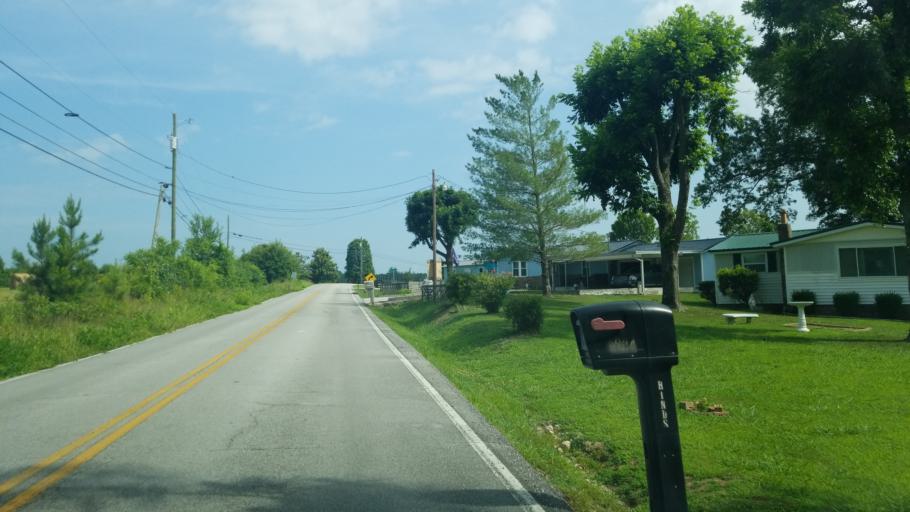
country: US
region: Tennessee
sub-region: Hamilton County
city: Apison
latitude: 35.0204
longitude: -85.0024
